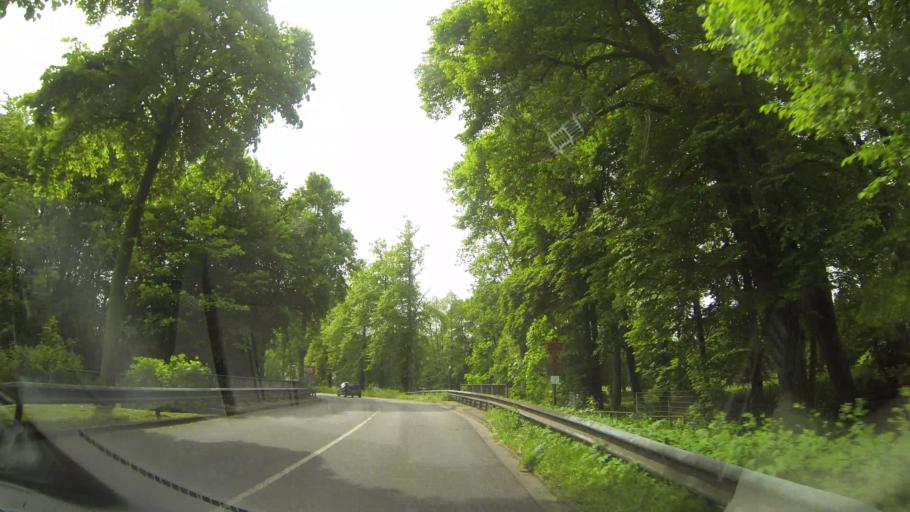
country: DE
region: Schleswig-Holstein
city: Rellingen
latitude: 53.6460
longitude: 9.8326
